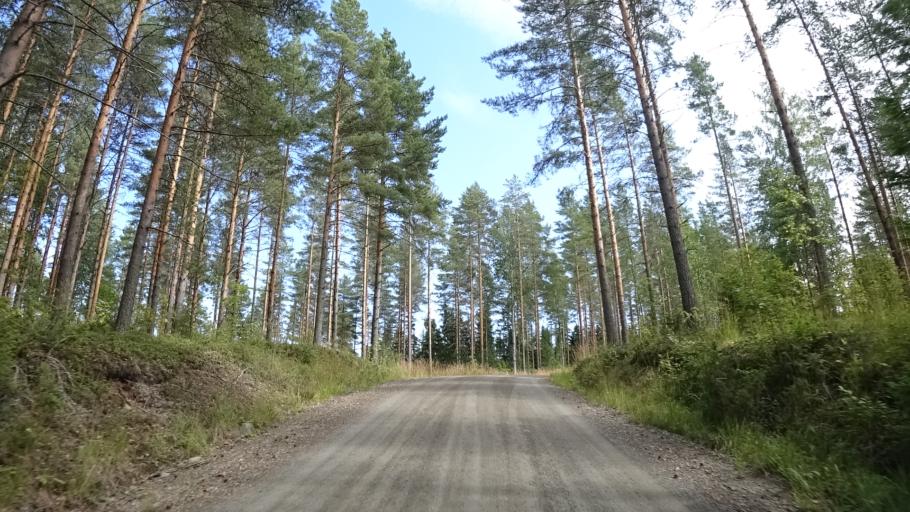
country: FI
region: North Karelia
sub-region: Joensuu
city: Pyhaeselkae
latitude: 62.3756
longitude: 29.8136
